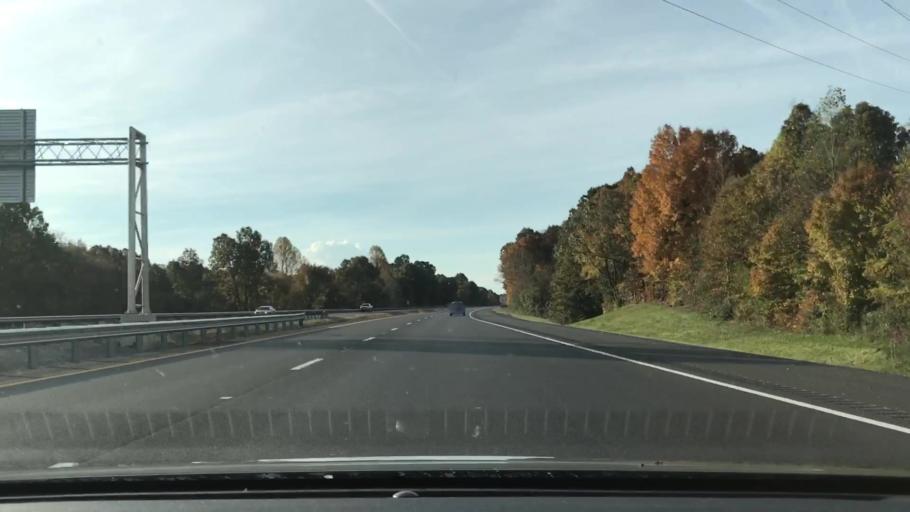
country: US
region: Kentucky
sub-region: Marshall County
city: Calvert City
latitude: 36.9799
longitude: -88.3458
